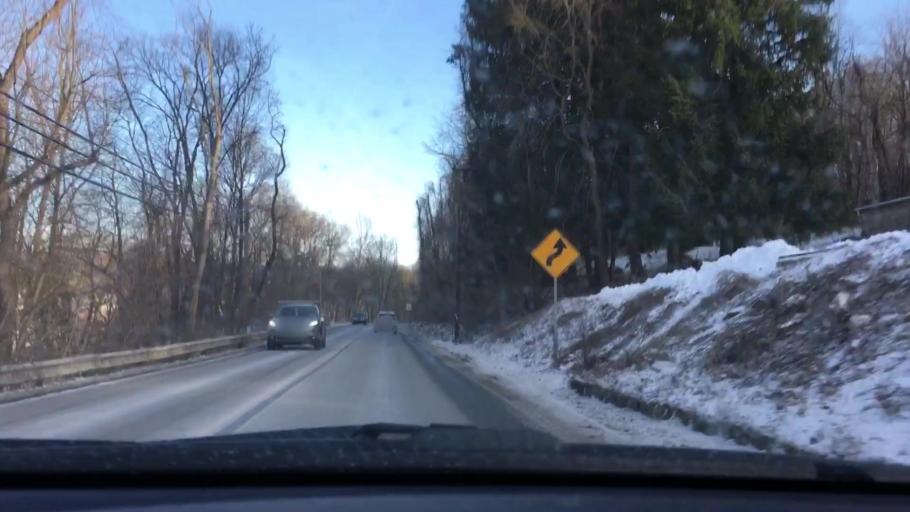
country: US
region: Pennsylvania
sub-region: Washington County
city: McMurray
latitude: 40.2784
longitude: -80.0775
